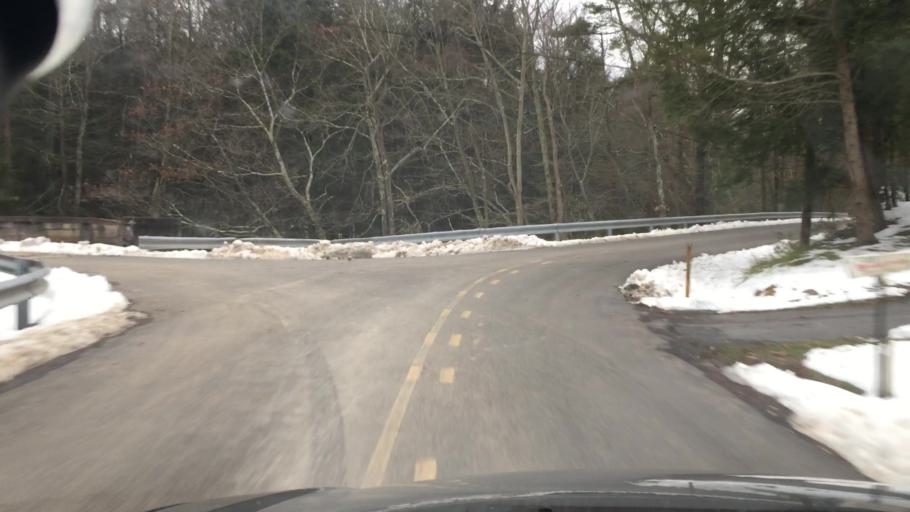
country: US
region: Pennsylvania
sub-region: Luzerne County
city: Conyngham
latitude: 41.0050
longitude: -76.1333
